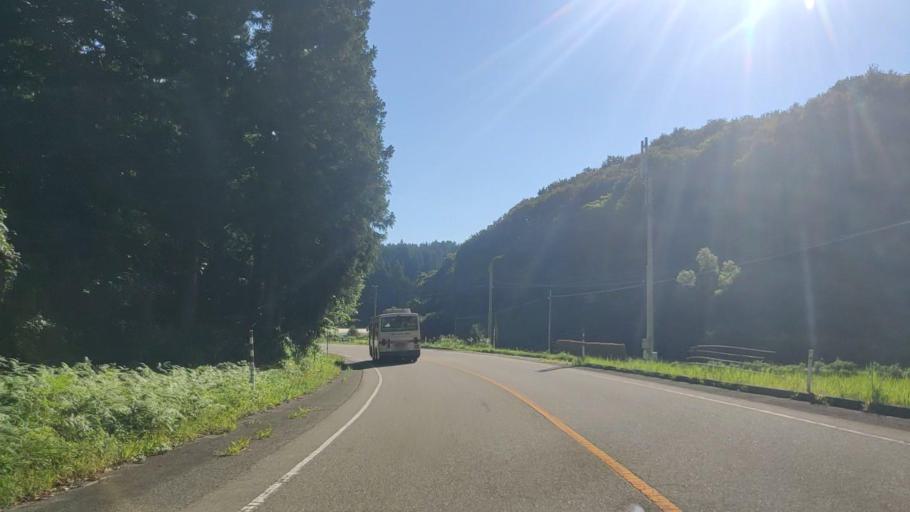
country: JP
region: Ishikawa
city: Nanao
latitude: 37.2438
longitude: 136.9884
